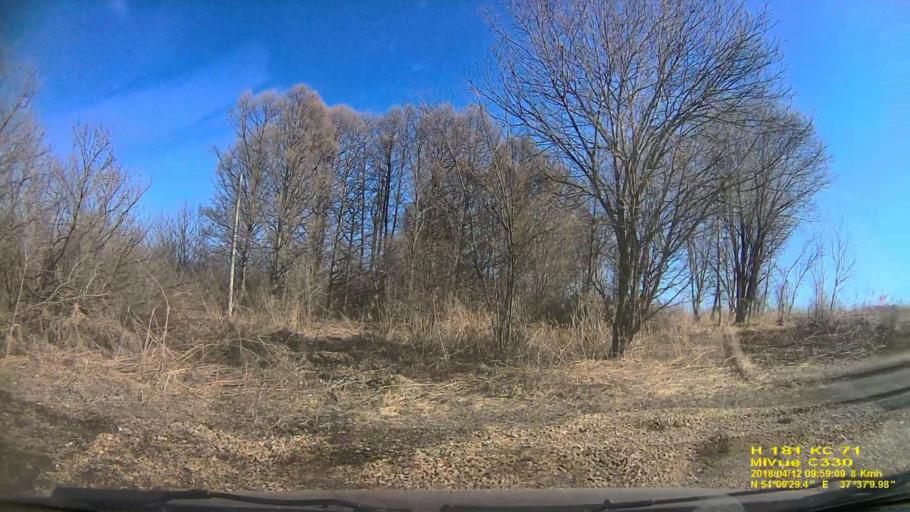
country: RU
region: Tula
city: Tula
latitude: 54.1582
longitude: 37.6195
